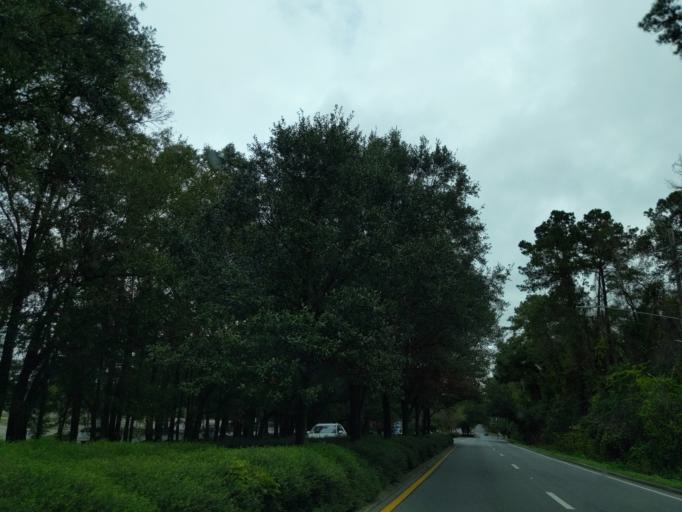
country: US
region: Florida
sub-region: Leon County
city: Tallahassee
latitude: 30.4353
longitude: -84.2495
